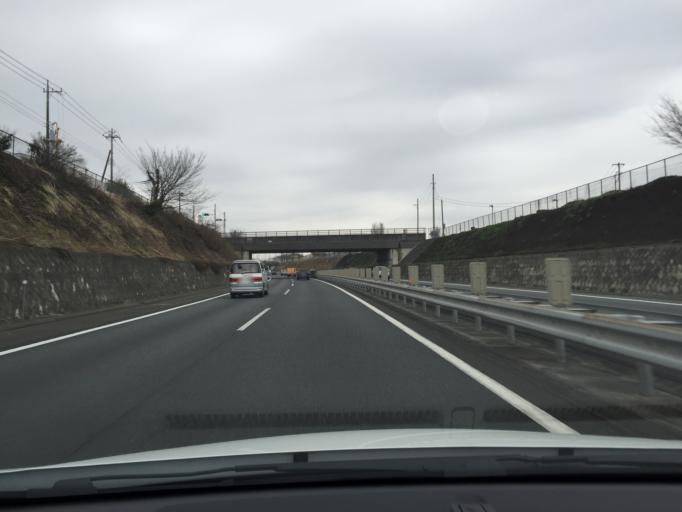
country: JP
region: Saitama
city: Hanno
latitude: 35.8142
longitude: 139.3611
